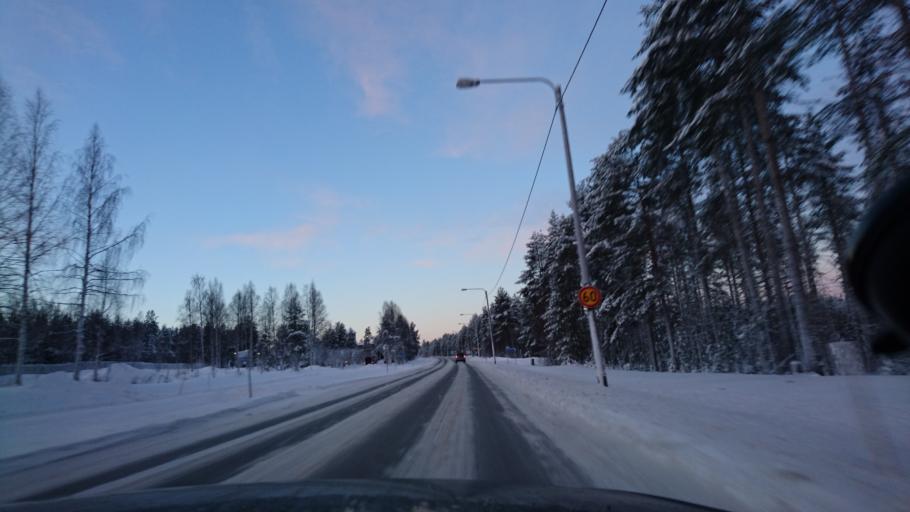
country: FI
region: Lapland
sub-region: Rovaniemi
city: Ranua
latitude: 65.9424
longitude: 26.4743
